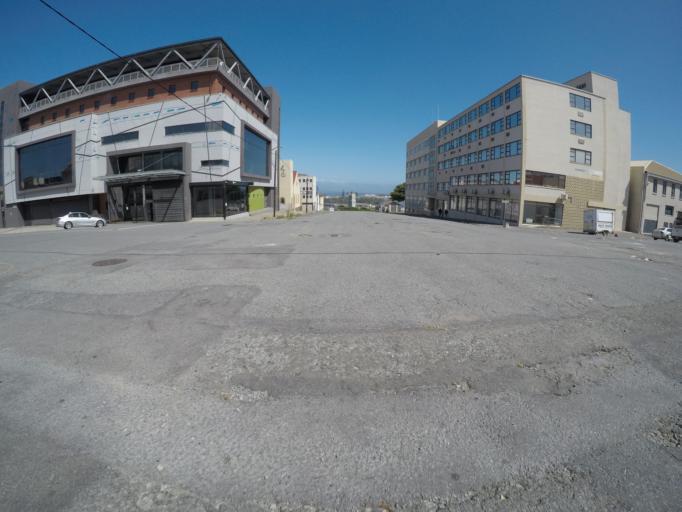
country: ZA
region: Eastern Cape
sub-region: Buffalo City Metropolitan Municipality
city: East London
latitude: -33.0209
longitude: 27.9060
